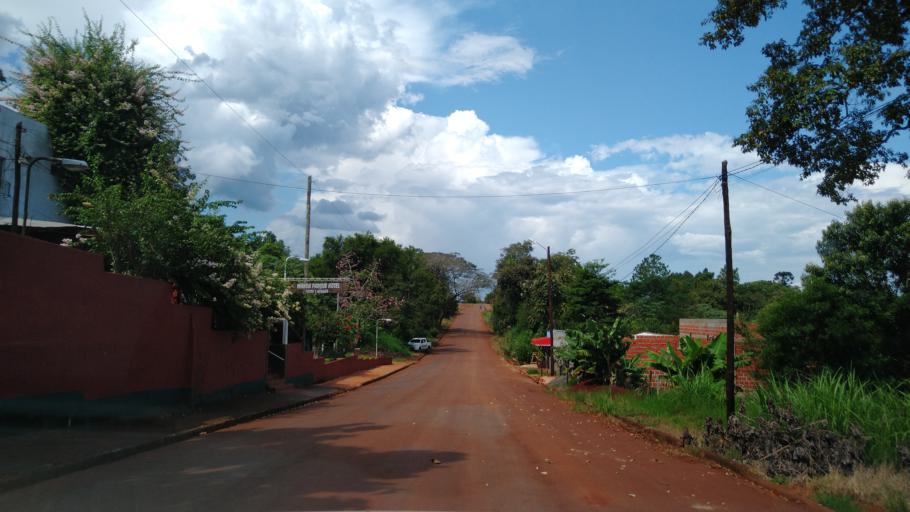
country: AR
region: Misiones
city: Puerto Libertad
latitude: -25.9663
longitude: -54.5964
